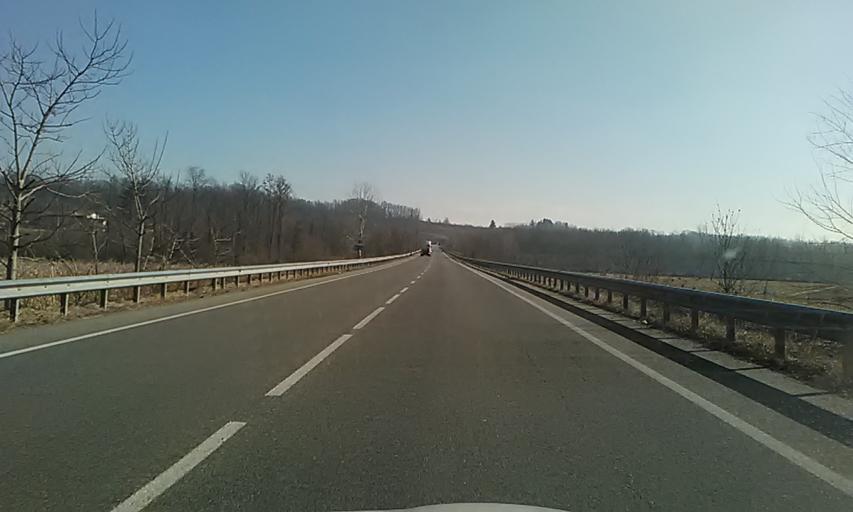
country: IT
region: Piedmont
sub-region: Provincia di Novara
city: Prato Sesia
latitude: 45.6595
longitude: 8.3730
